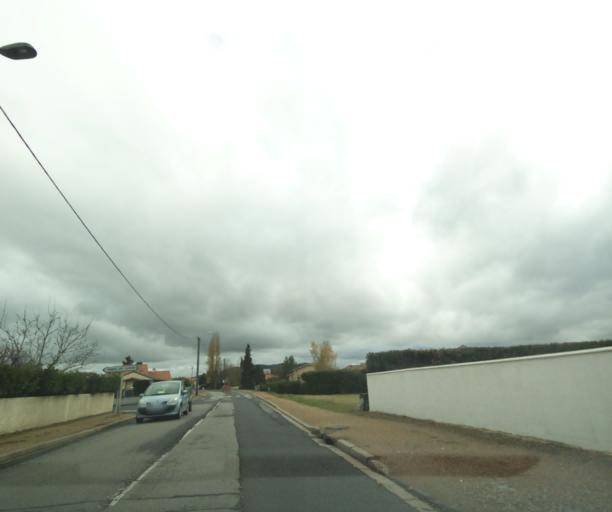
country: FR
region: Auvergne
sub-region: Departement du Puy-de-Dome
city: Pont-du-Chateau
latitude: 45.8080
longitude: 3.2430
